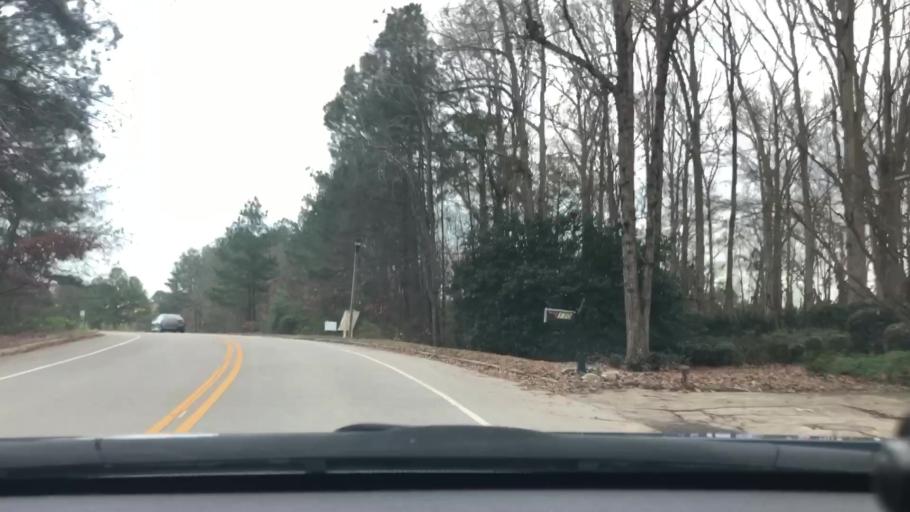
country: US
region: South Carolina
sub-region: Lexington County
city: Irmo
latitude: 34.0766
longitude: -81.1642
